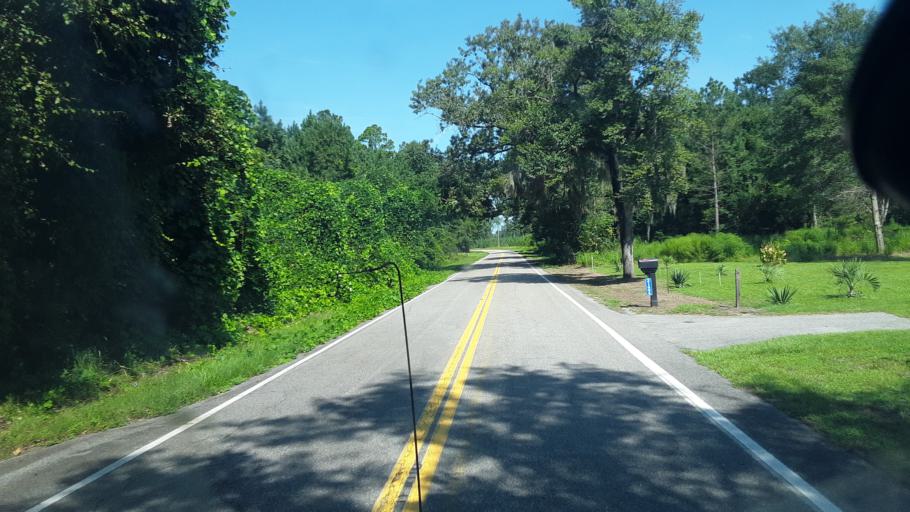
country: US
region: South Carolina
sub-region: Hampton County
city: Varnville
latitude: 32.9495
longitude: -81.0335
